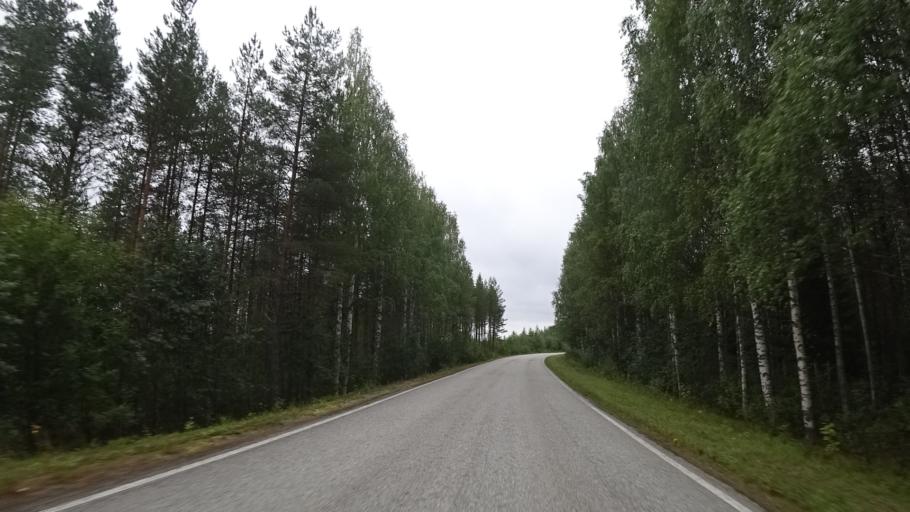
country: FI
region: North Karelia
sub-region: Pielisen Karjala
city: Lieksa
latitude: 63.3510
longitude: 30.2655
